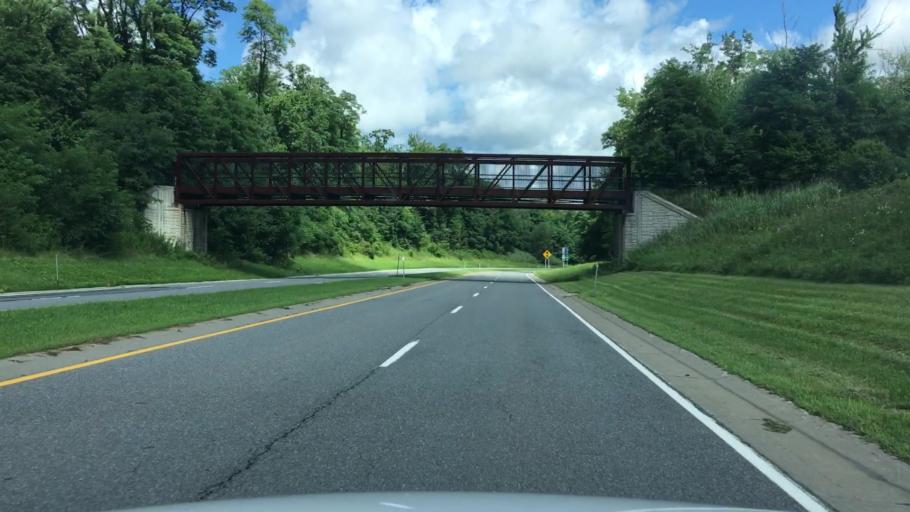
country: US
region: New York
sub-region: Albany County
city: Colonie
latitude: 42.7429
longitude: -73.8184
